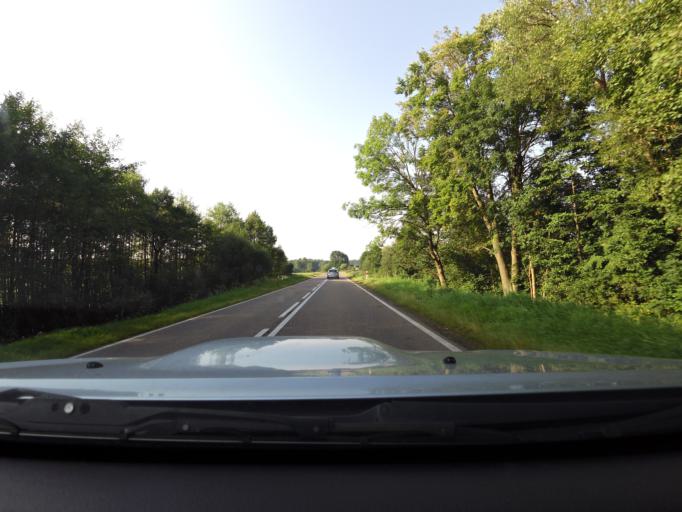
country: LT
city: Lazdijai
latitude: 54.1357
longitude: 23.4648
